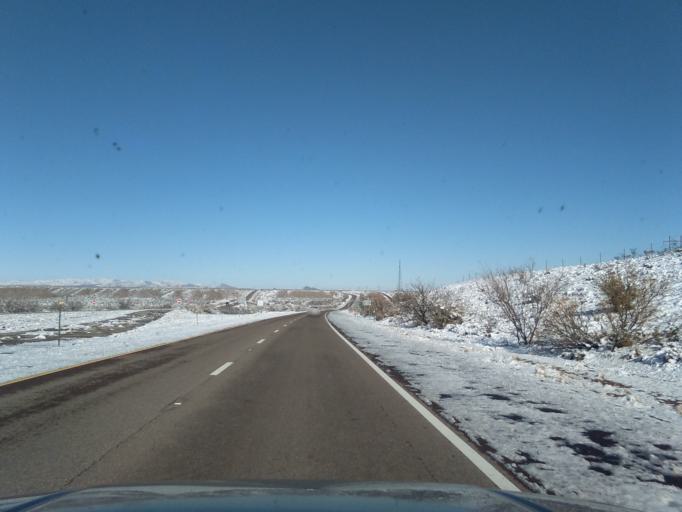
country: US
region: New Mexico
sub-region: Socorro County
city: Socorro
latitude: 33.6554
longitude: -107.0993
